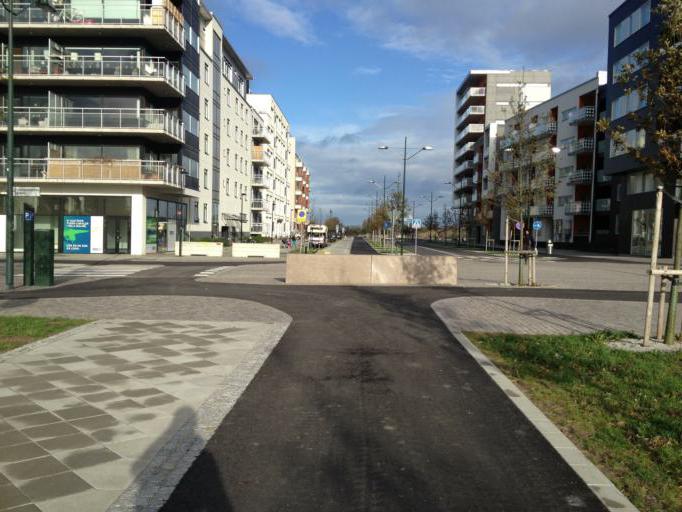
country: SE
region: Skane
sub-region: Malmo
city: Malmoe
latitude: 55.6155
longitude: 12.9805
